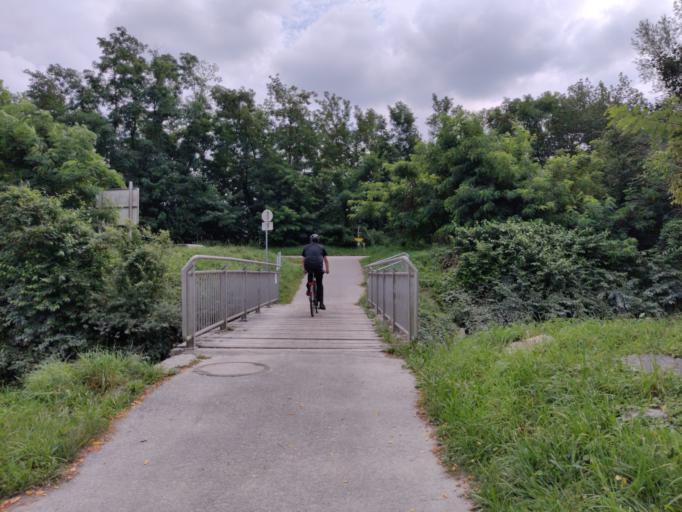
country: AT
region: Lower Austria
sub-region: Politischer Bezirk Melk
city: Melk
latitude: 48.2296
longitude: 15.3126
